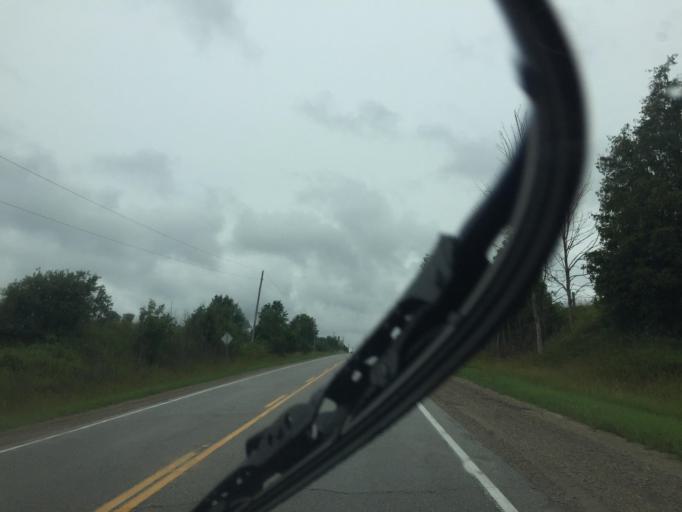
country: CA
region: Ontario
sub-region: Wellington County
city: Guelph
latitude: 43.4703
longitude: -80.2239
